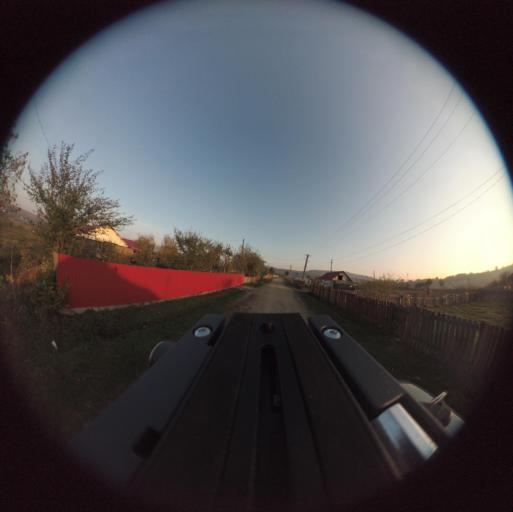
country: RO
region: Vaslui
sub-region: Comuna Bacesti
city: Bacesti
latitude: 46.8313
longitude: 27.2466
